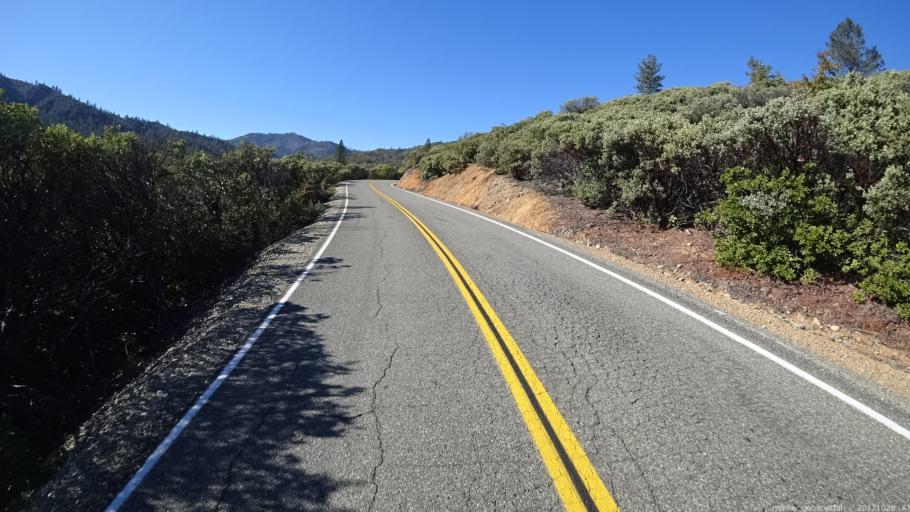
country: US
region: California
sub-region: Shasta County
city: Shasta
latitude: 40.6619
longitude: -122.4719
